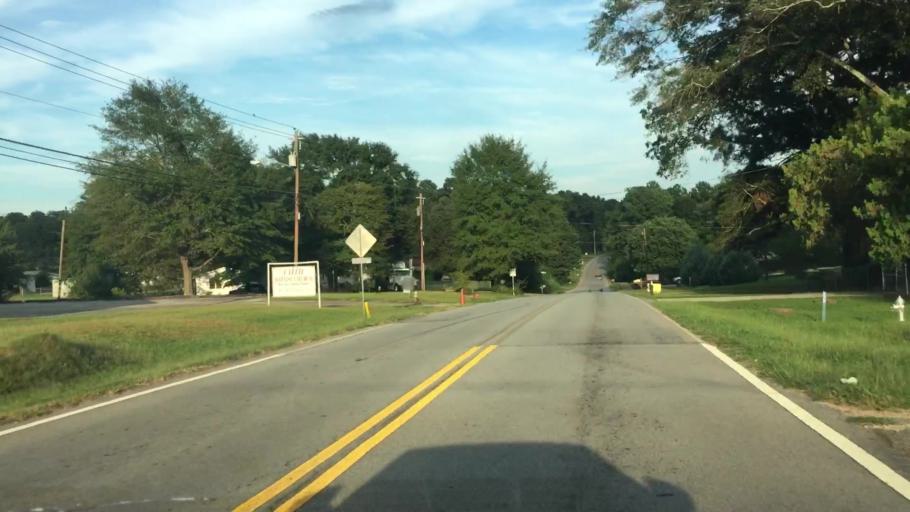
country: US
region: Georgia
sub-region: Henry County
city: Stockbridge
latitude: 33.5405
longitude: -84.1927
